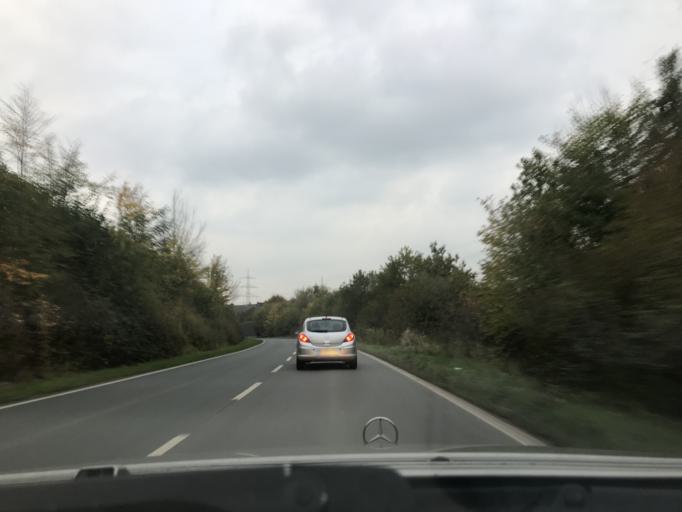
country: DE
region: North Rhine-Westphalia
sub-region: Regierungsbezirk Munster
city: Gelsenkirchen
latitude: 51.5289
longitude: 7.1291
